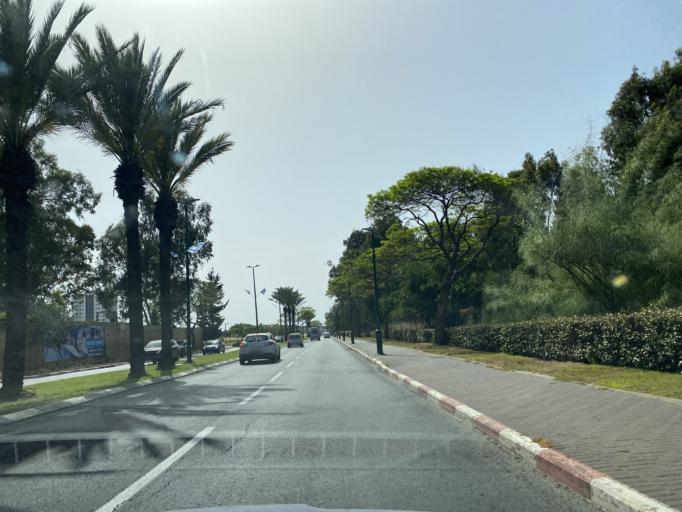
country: IL
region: Tel Aviv
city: Herzliyya
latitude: 32.1779
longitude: 34.8356
